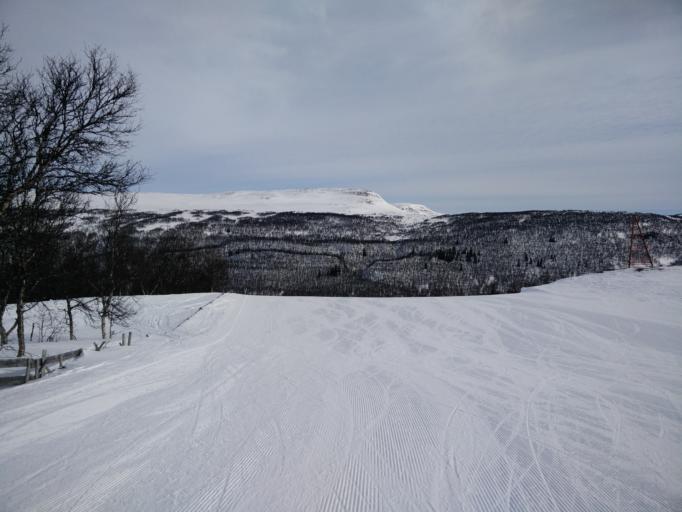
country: NO
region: Sor-Trondelag
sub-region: Tydal
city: Aas
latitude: 62.7009
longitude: 12.3738
